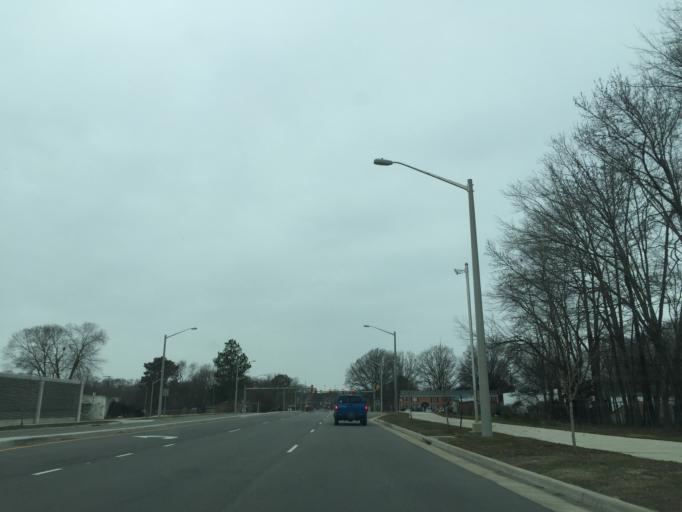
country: US
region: Virginia
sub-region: City of Newport News
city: Newport News
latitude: 37.0864
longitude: -76.4947
